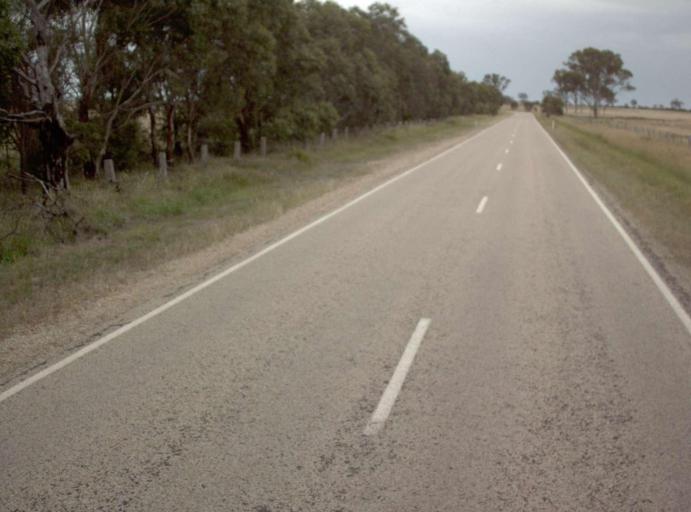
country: AU
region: Victoria
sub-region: East Gippsland
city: Bairnsdale
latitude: -37.8998
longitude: 147.5533
